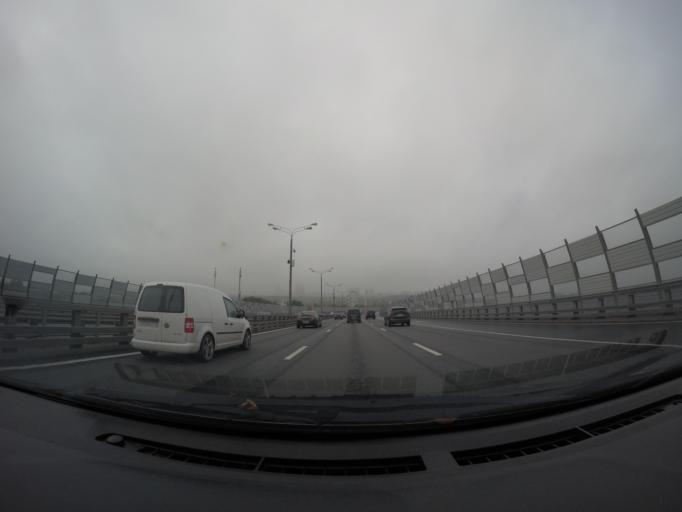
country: RU
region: Moscow
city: Shchukino
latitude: 55.7749
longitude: 37.4402
